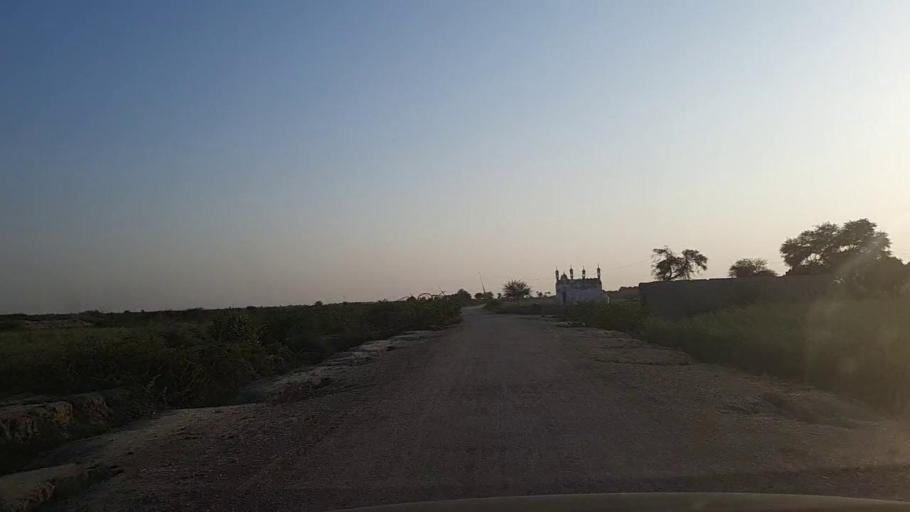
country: PK
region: Sindh
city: Naukot
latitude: 24.8352
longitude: 69.3087
